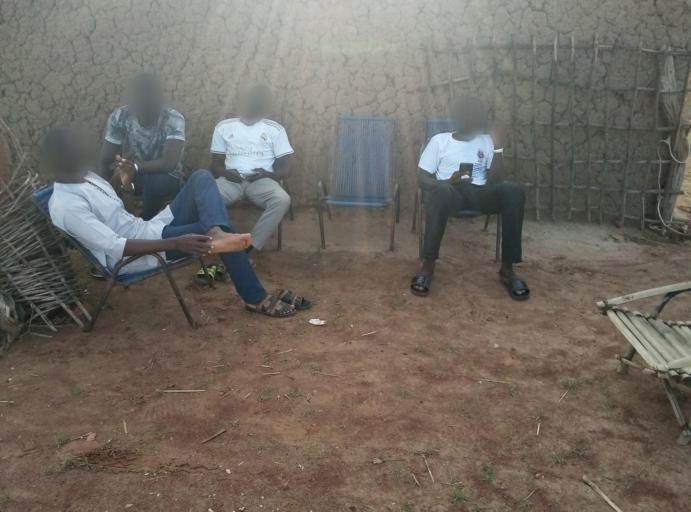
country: ML
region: Segou
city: San
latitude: 13.1149
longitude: -5.3121
